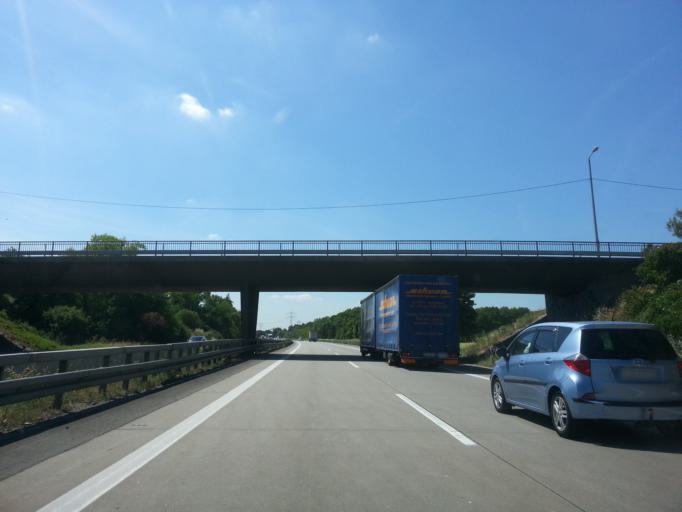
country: DE
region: Baden-Wuerttemberg
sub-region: Karlsruhe Region
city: Bruhl
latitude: 49.4368
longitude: 8.5402
